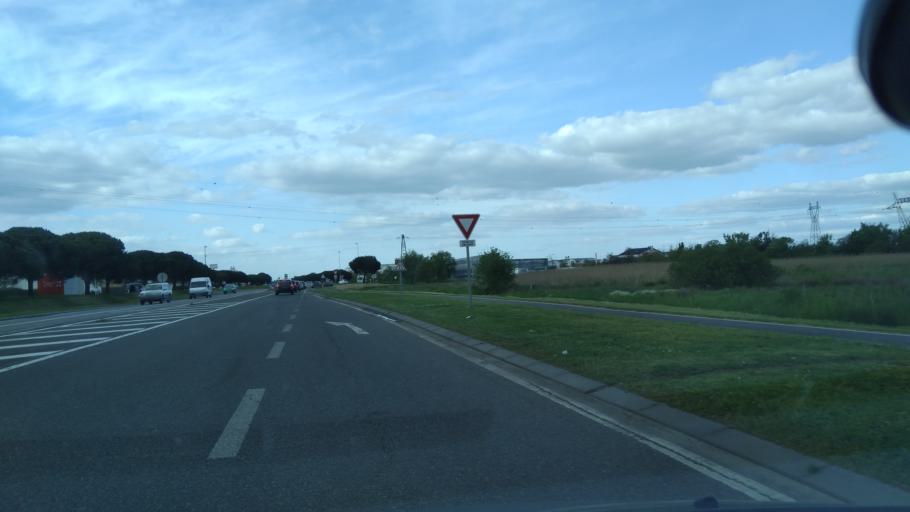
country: FR
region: Pays de la Loire
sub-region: Departement de la Loire-Atlantique
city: Saint-Nazaire
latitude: 47.2915
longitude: -2.2088
